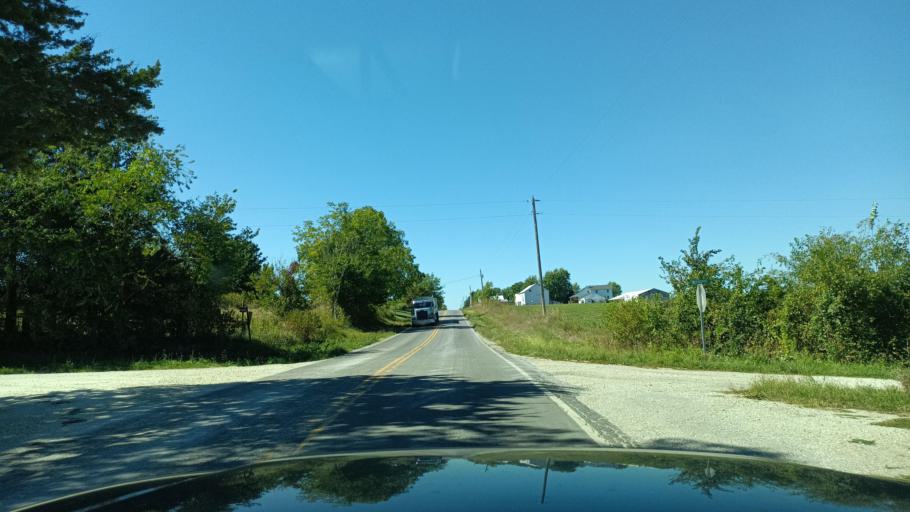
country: US
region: Missouri
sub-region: Macon County
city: La Plata
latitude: 40.0221
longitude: -92.5473
